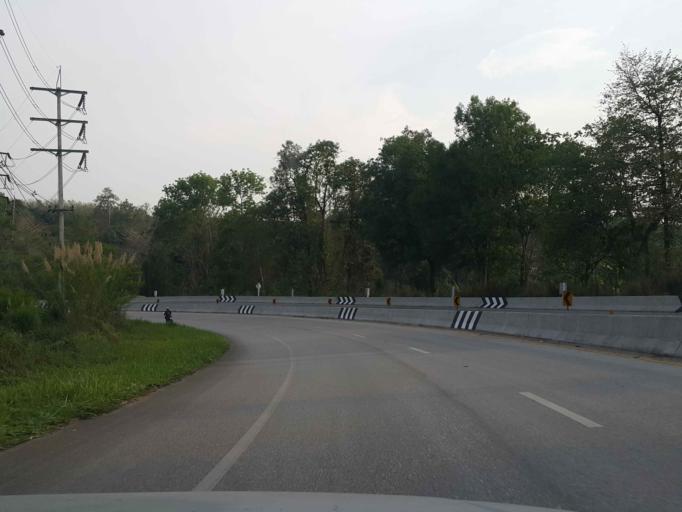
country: TH
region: Chiang Mai
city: Mae Taeng
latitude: 19.2005
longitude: 98.9643
